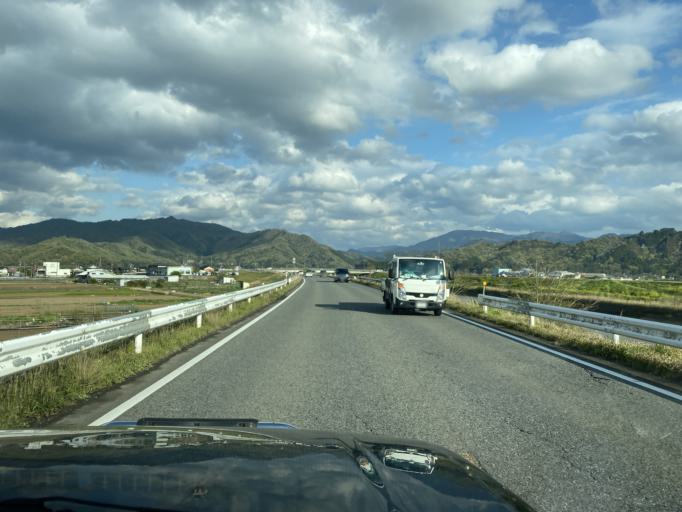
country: JP
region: Hyogo
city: Toyooka
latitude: 35.4910
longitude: 134.8441
